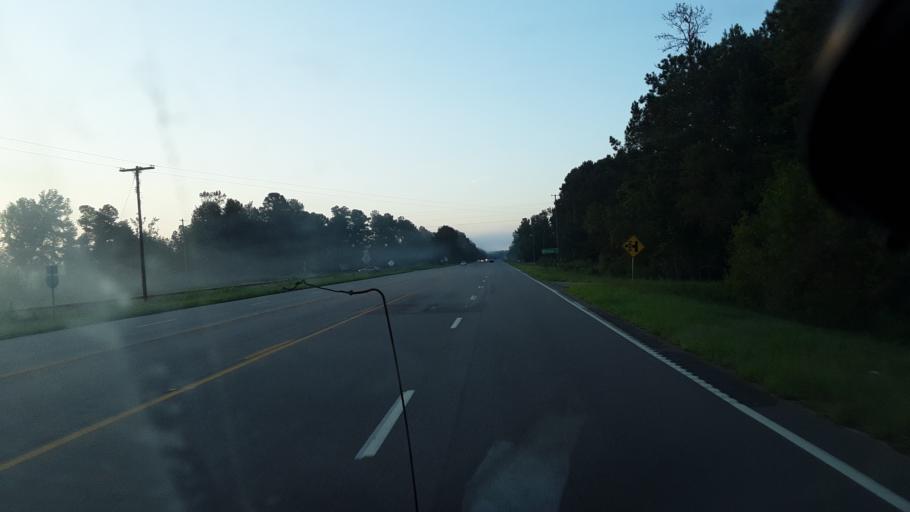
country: US
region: South Carolina
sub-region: Clarendon County
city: Manning
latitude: 33.7353
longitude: -80.2054
